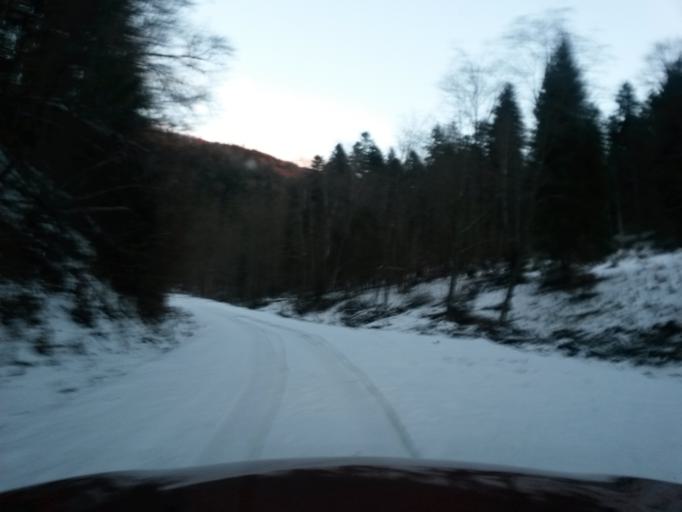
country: SK
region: Kosicky
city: Medzev
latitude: 48.7854
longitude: 20.8360
